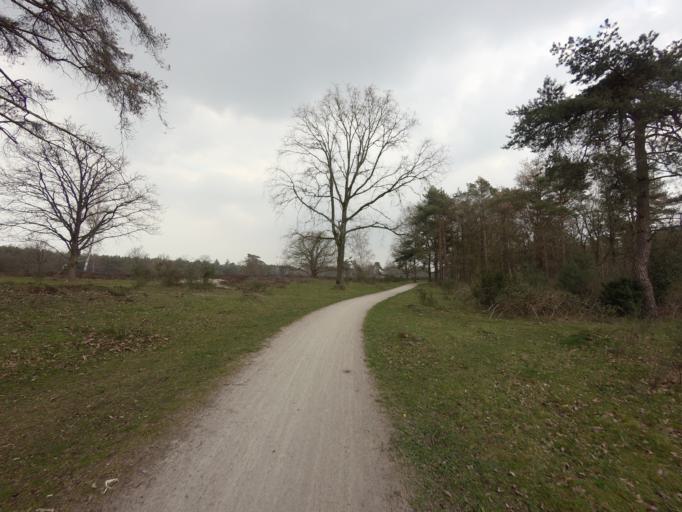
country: NL
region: North Holland
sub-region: Gemeente Huizen
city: Huizen
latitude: 52.2953
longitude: 5.2044
